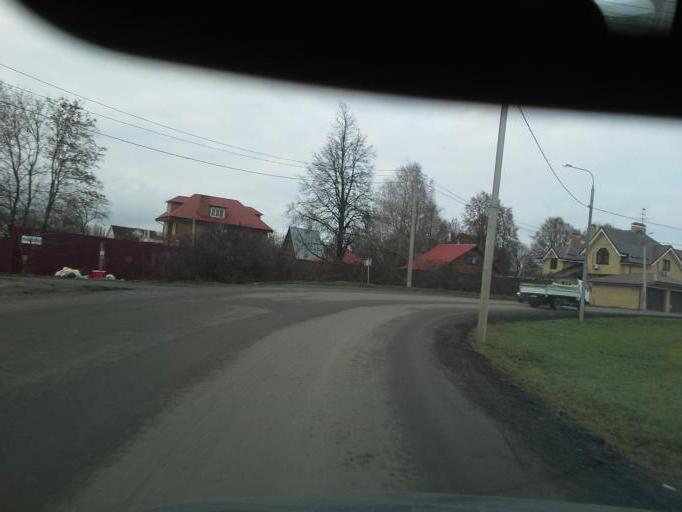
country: RU
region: Moskovskaya
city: Kommunarka
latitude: 55.5588
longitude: 37.4195
